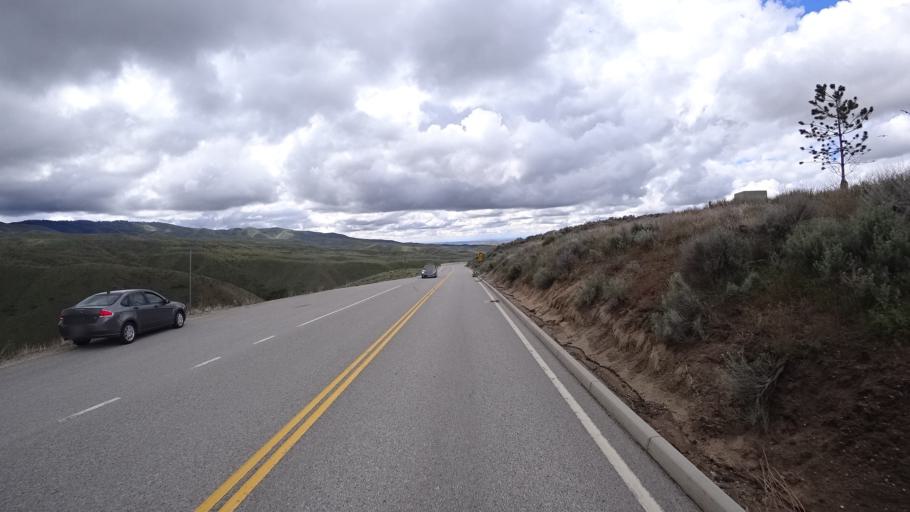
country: US
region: Idaho
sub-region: Ada County
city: Boise
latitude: 43.7016
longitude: -116.1633
